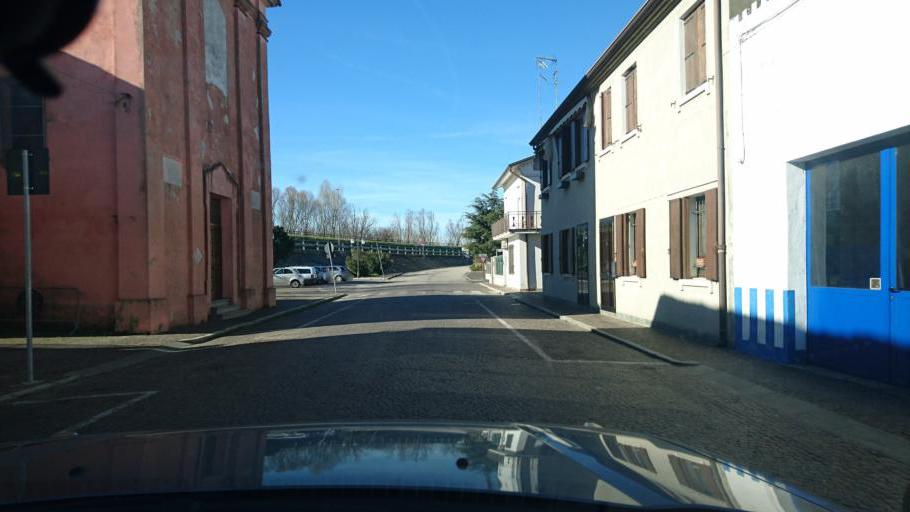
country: IT
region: Veneto
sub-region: Provincia di Rovigo
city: Ariano
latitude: 44.9463
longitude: 12.1192
